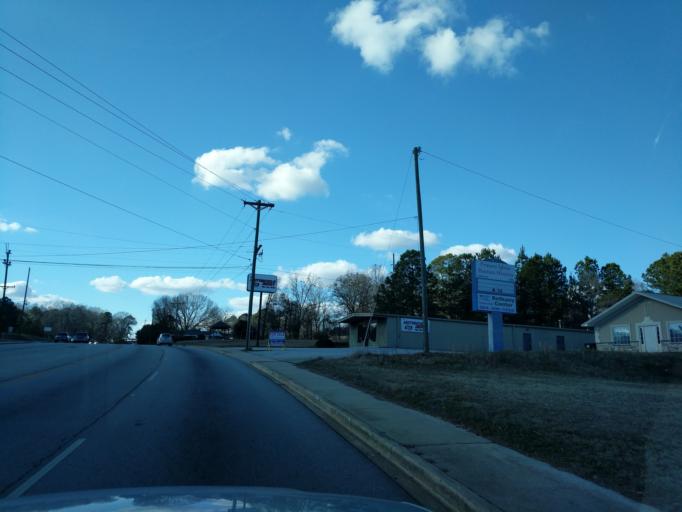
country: US
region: South Carolina
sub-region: Greenwood County
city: Greenwood
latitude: 34.2058
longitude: -82.1377
